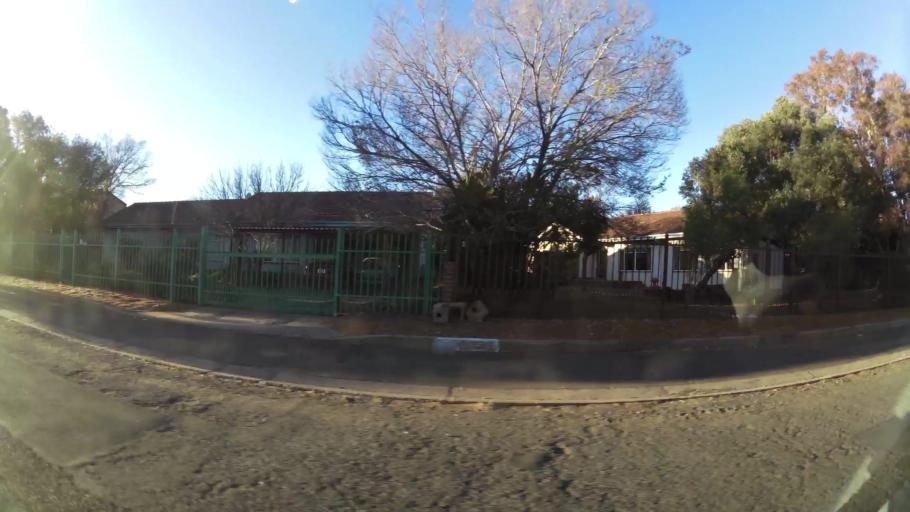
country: ZA
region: Northern Cape
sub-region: Frances Baard District Municipality
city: Kimberley
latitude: -28.7637
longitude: 24.7412
